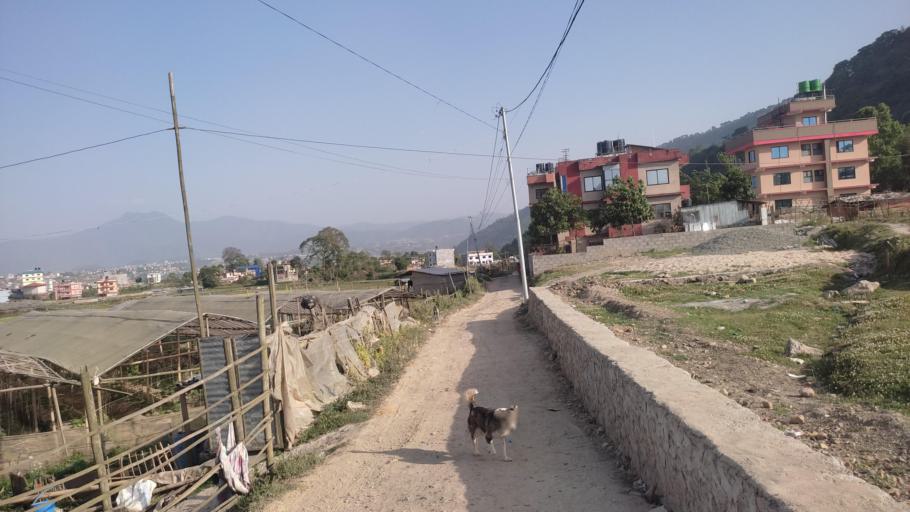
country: NP
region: Central Region
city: Kirtipur
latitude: 27.6585
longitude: 85.2707
